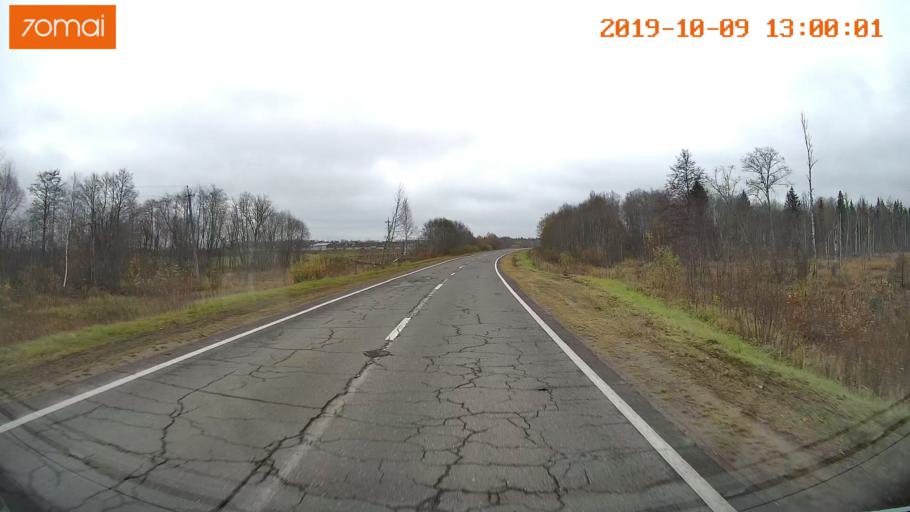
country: RU
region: Jaroslavl
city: Prechistoye
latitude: 58.3806
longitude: 40.4744
